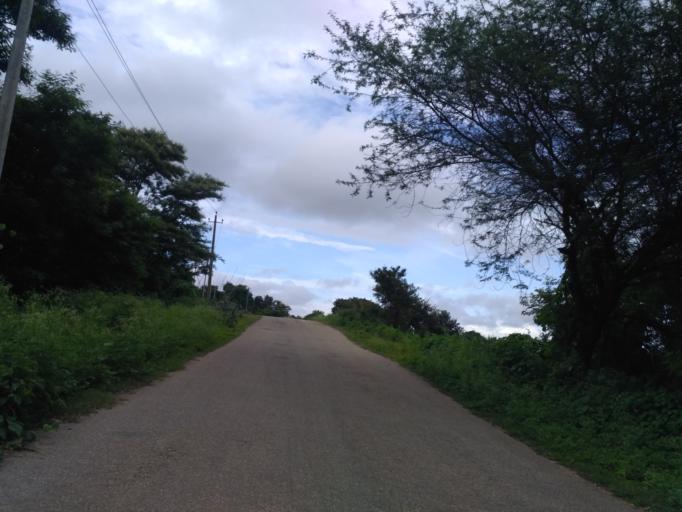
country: IN
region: Karnataka
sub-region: Hassan
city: Gorur
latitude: 12.8331
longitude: 76.0988
